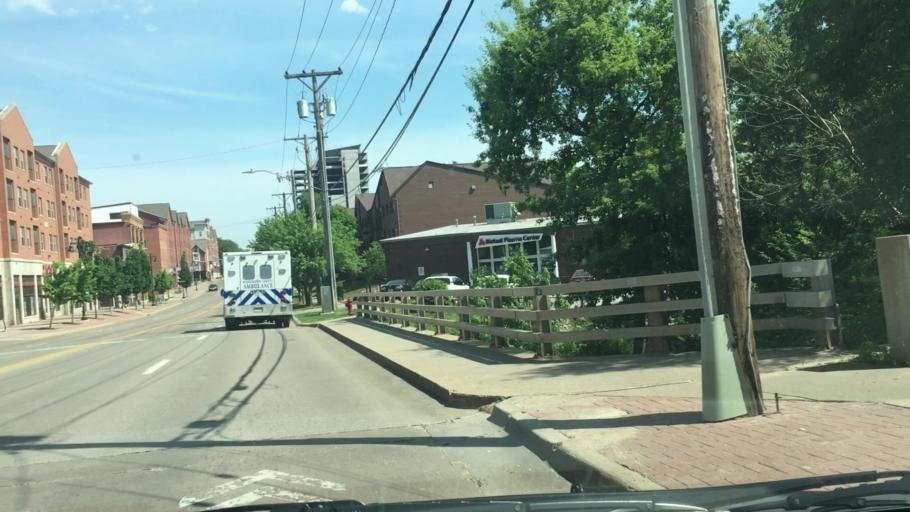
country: US
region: Iowa
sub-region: Johnson County
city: Iowa City
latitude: 41.6553
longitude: -91.5302
